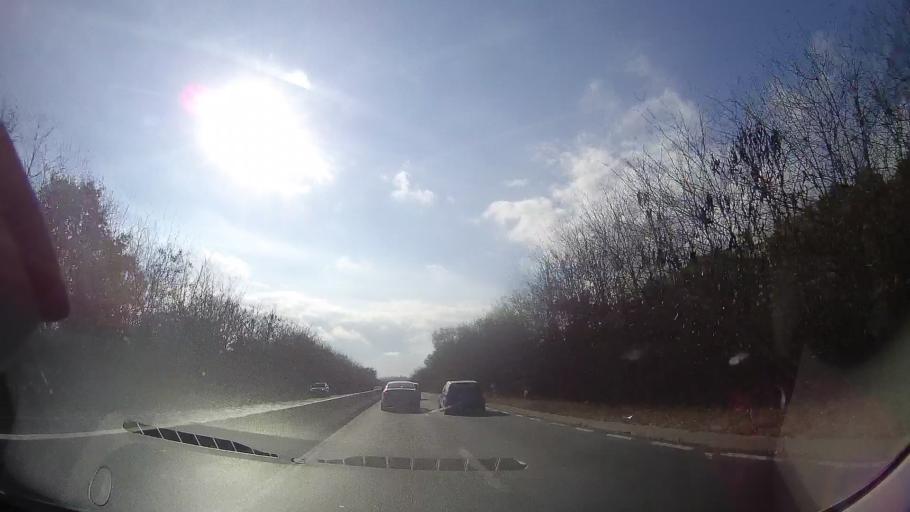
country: RO
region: Constanta
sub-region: Comuna Agigea
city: Agigea
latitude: 44.1252
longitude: 28.6144
